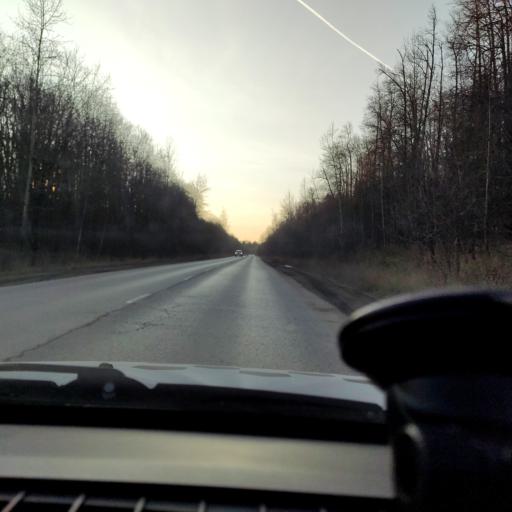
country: RU
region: Perm
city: Froly
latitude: 57.9567
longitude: 56.3145
